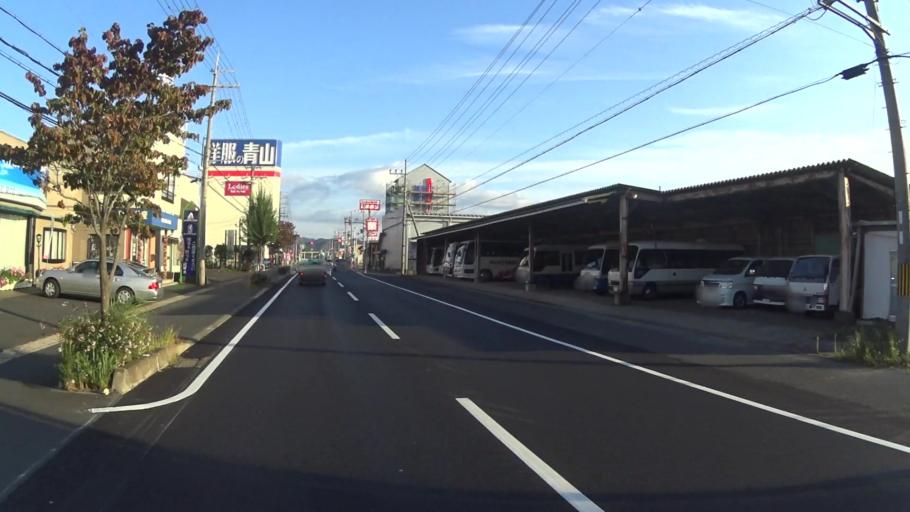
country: JP
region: Kyoto
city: Miyazu
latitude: 35.6058
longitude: 135.0826
